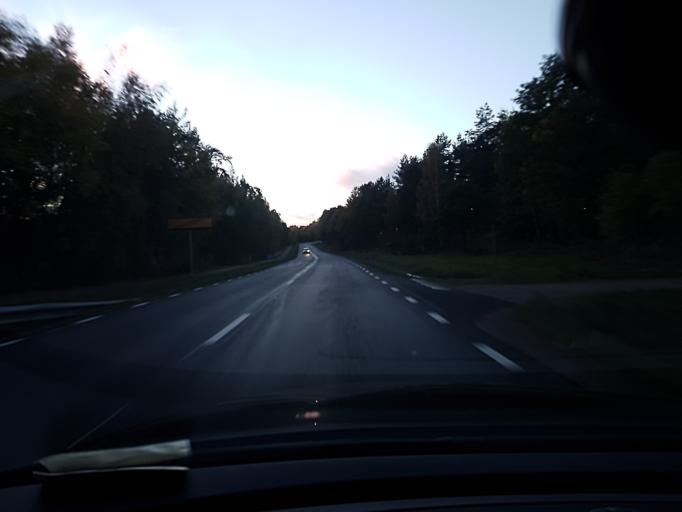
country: SE
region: Halland
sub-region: Laholms Kommun
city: Veinge
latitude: 56.7198
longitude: 13.1414
